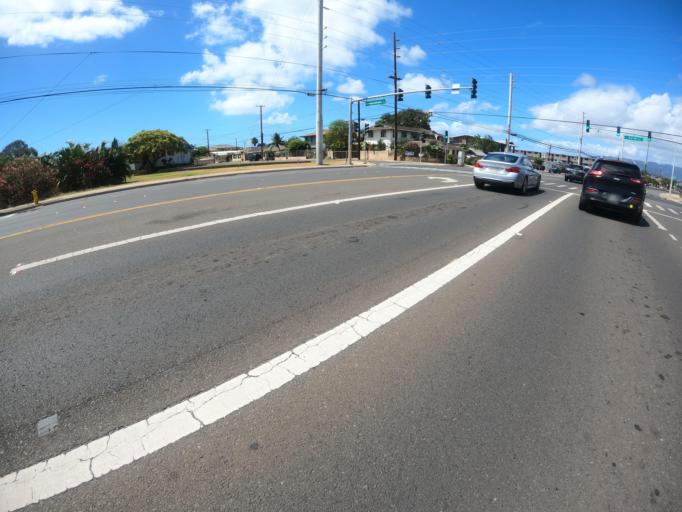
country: US
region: Hawaii
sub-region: Honolulu County
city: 'Ewa Beach
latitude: 21.3124
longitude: -158.0100
